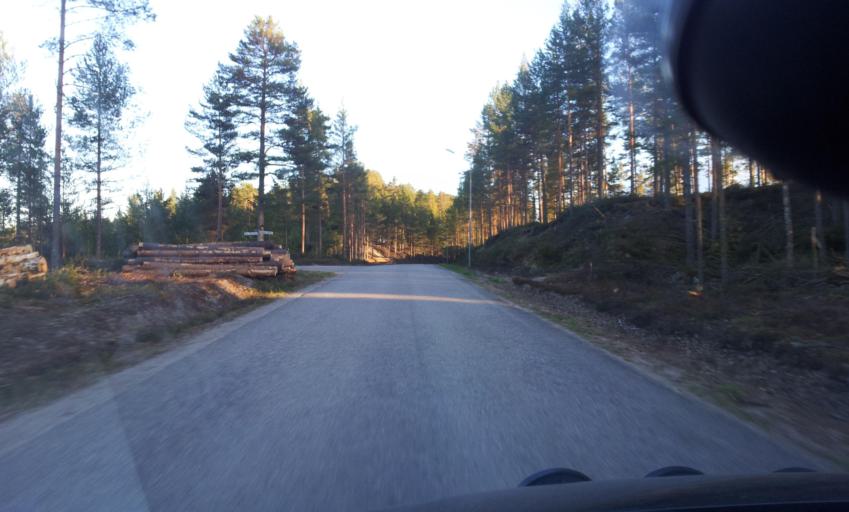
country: SE
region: Gaevleborg
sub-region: Bollnas Kommun
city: Kilafors
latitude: 61.3912
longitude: 16.6104
